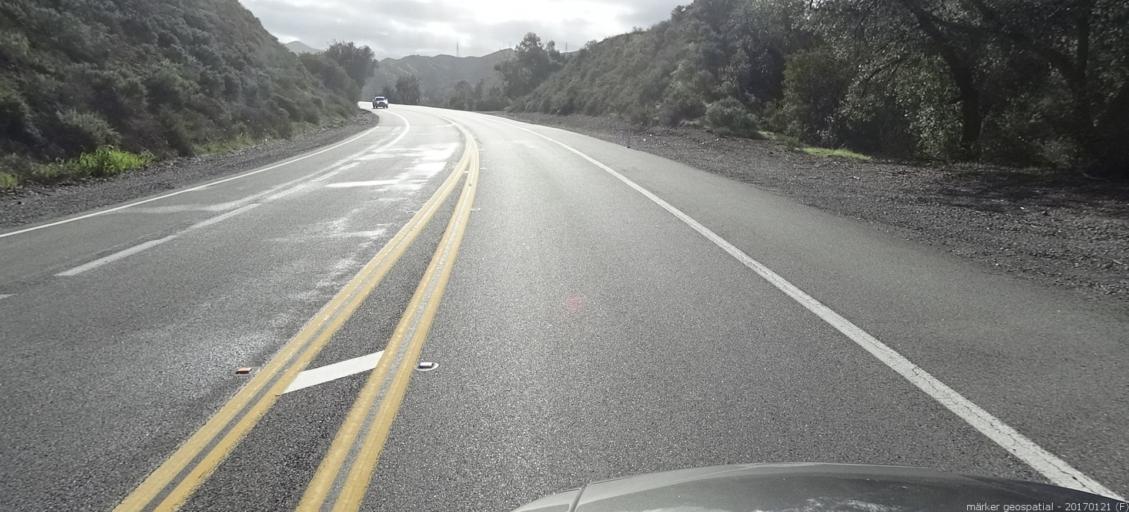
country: US
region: California
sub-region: Orange County
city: Foothill Ranch
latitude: 33.7422
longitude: -117.6677
